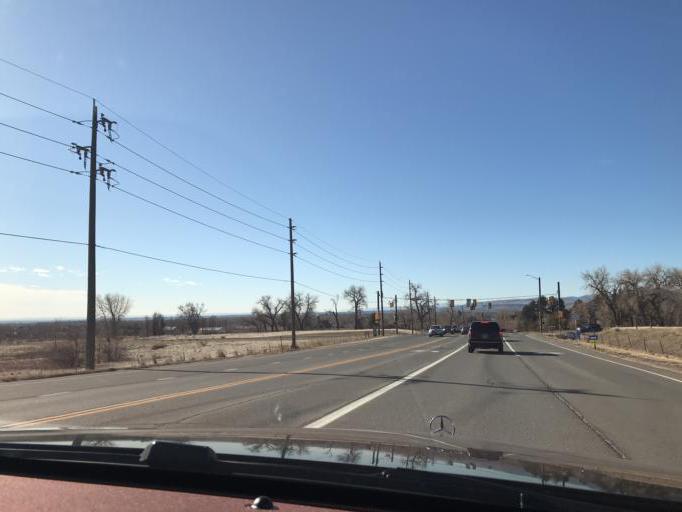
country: US
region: Colorado
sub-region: Jefferson County
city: Applewood
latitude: 39.8446
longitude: -105.1653
